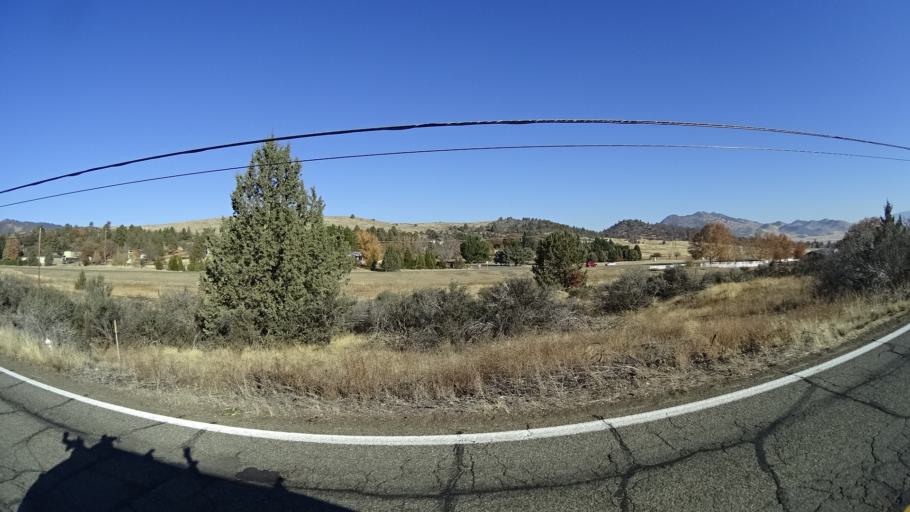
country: US
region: California
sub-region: Siskiyou County
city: Yreka
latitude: 41.7393
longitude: -122.6113
